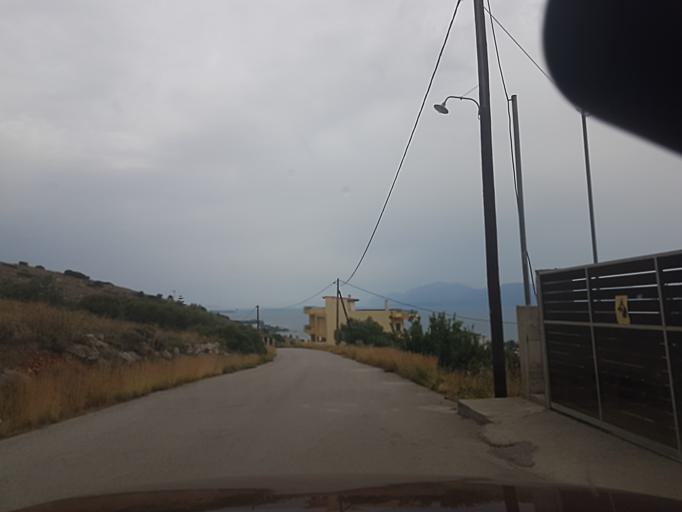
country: GR
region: Central Greece
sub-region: Nomos Evvoias
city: Chalkida
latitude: 38.4615
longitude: 23.6268
